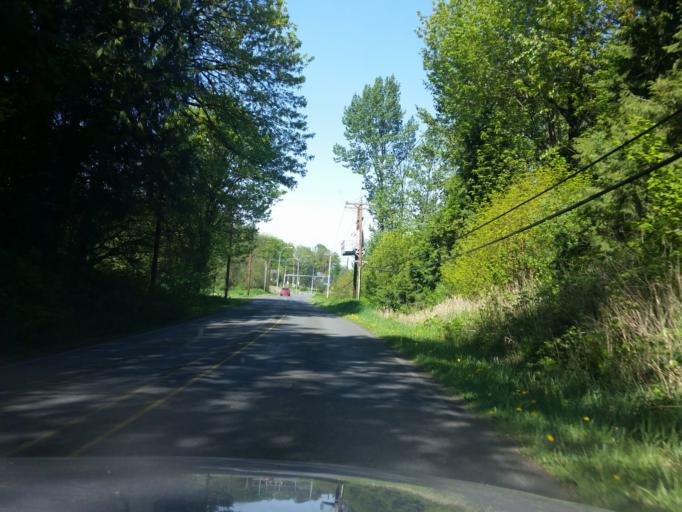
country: US
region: Washington
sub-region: Snohomish County
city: Cathcart
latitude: 47.8774
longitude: -122.1061
